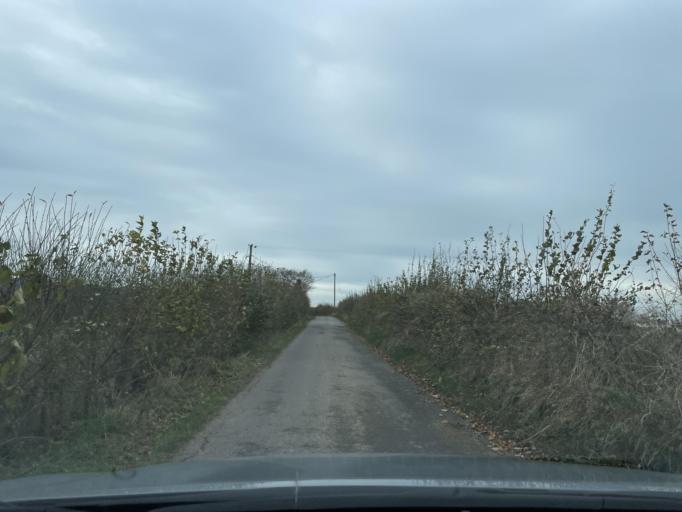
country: GB
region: England
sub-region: Borough of Swindon
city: Wroughton
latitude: 51.5139
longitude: -1.8235
